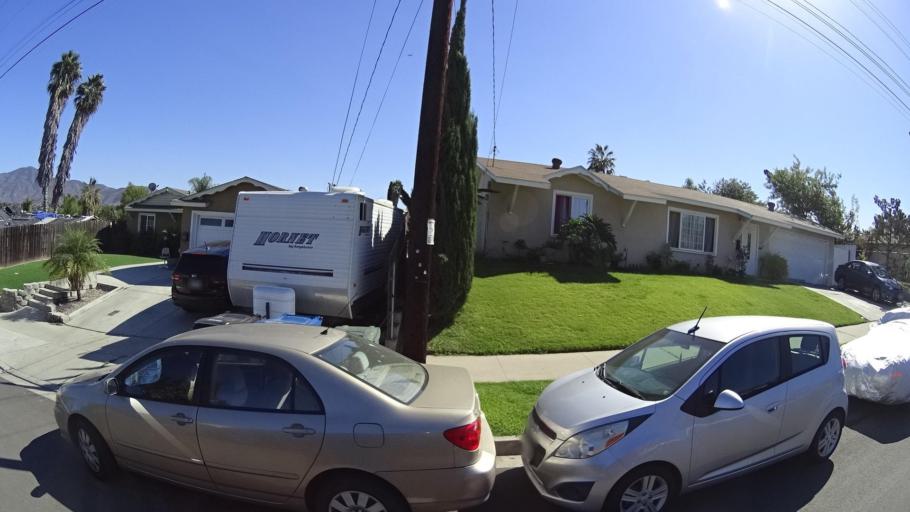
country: US
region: California
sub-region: San Diego County
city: La Presa
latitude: 32.7078
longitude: -117.0172
